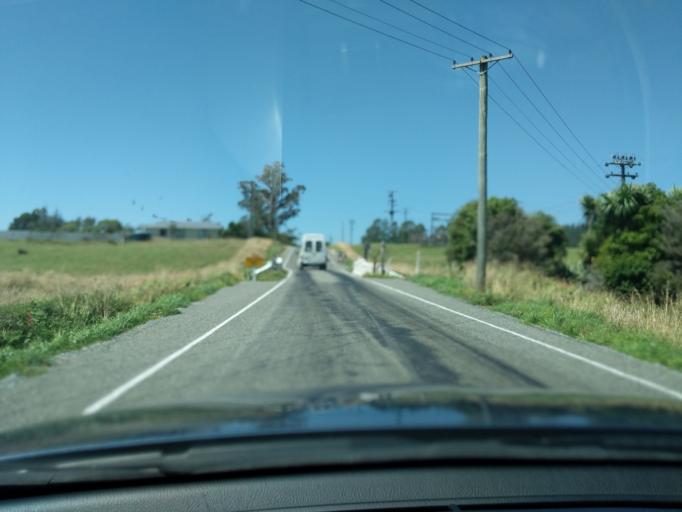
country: NZ
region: Tasman
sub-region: Tasman District
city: Takaka
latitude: -40.6869
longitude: 172.6507
